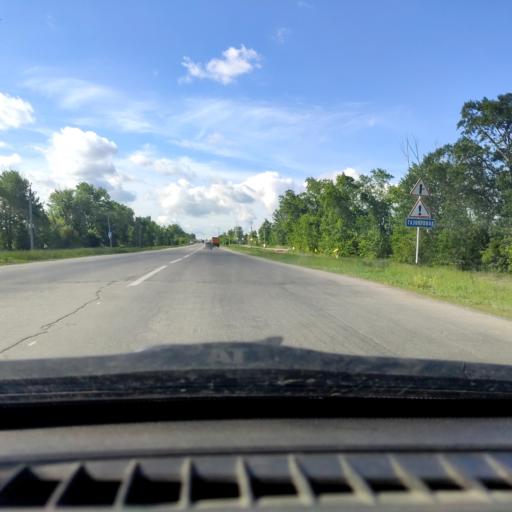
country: RU
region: Samara
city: Tol'yatti
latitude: 53.5905
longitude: 49.4062
